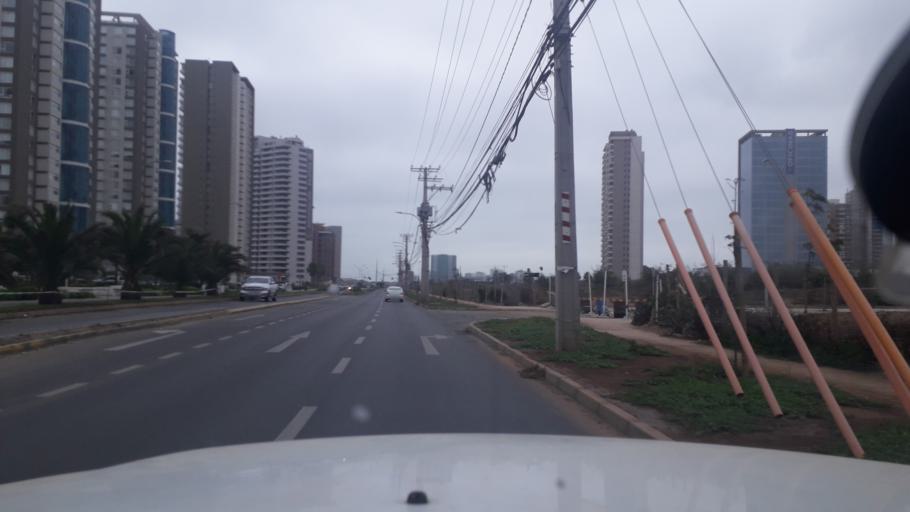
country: CL
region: Valparaiso
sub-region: Provincia de Valparaiso
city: Vina del Mar
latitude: -32.9525
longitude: -71.5440
